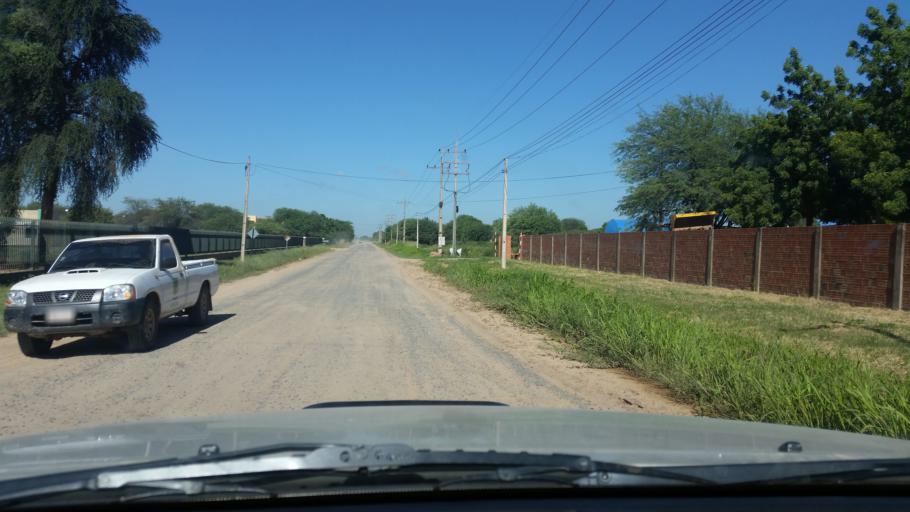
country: PY
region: Boqueron
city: Colonia Menno
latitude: -22.3980
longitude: -59.8368
